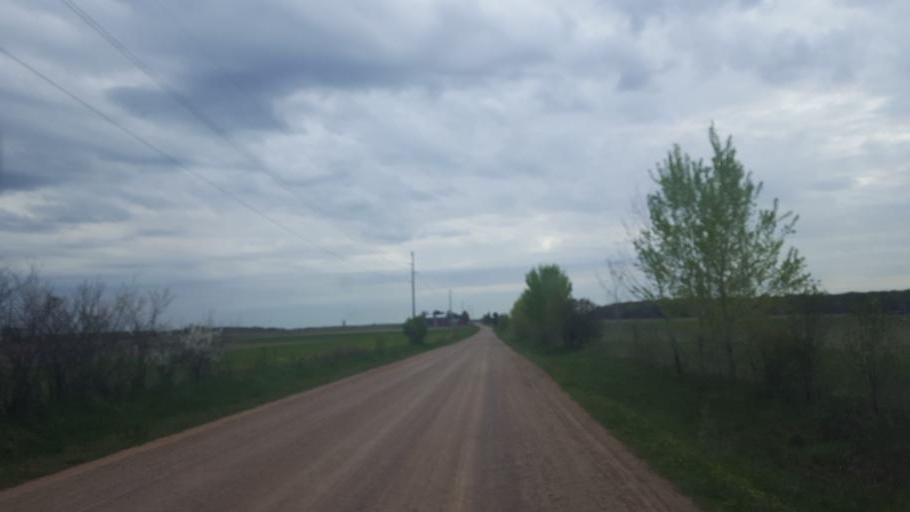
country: US
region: Wisconsin
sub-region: Marathon County
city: Spencer
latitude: 44.6289
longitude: -90.3766
